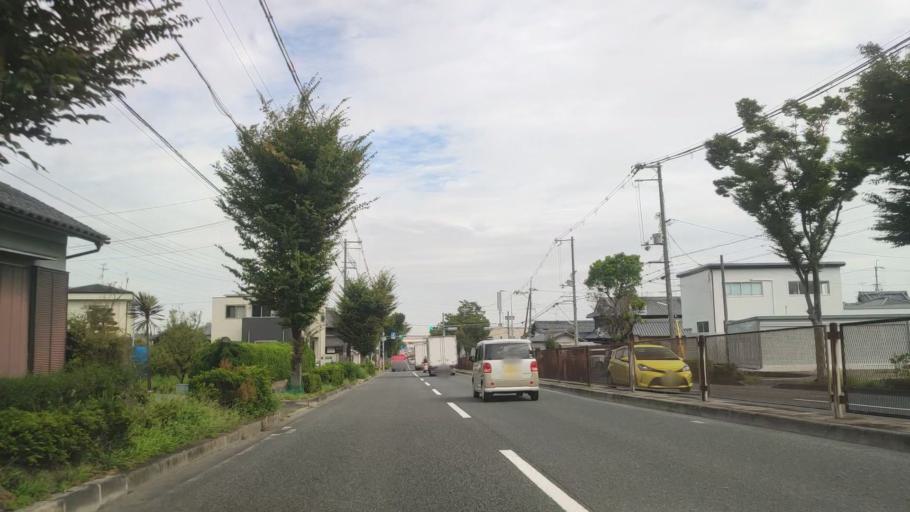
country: JP
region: Osaka
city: Tondabayashicho
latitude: 34.5272
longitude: 135.6049
